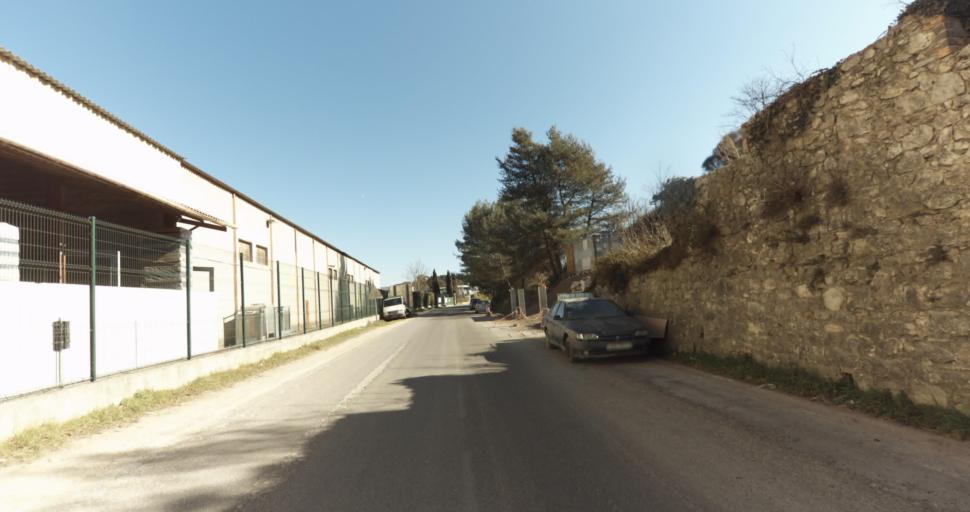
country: FR
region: Provence-Alpes-Cote d'Azur
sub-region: Departement des Bouches-du-Rhone
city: Cadolive
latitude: 43.3998
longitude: 5.5597
